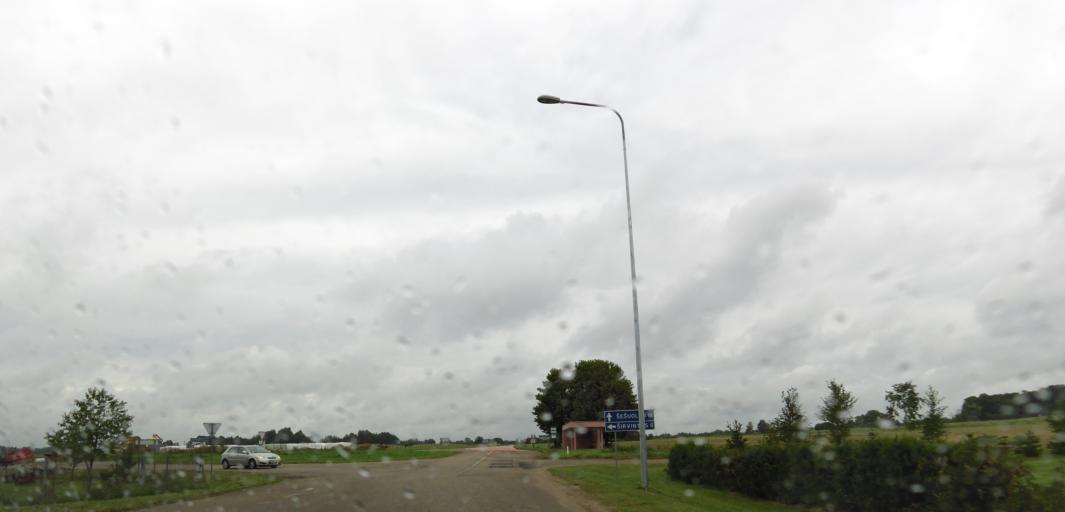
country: LT
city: Sirvintos
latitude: 55.0890
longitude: 24.9943
